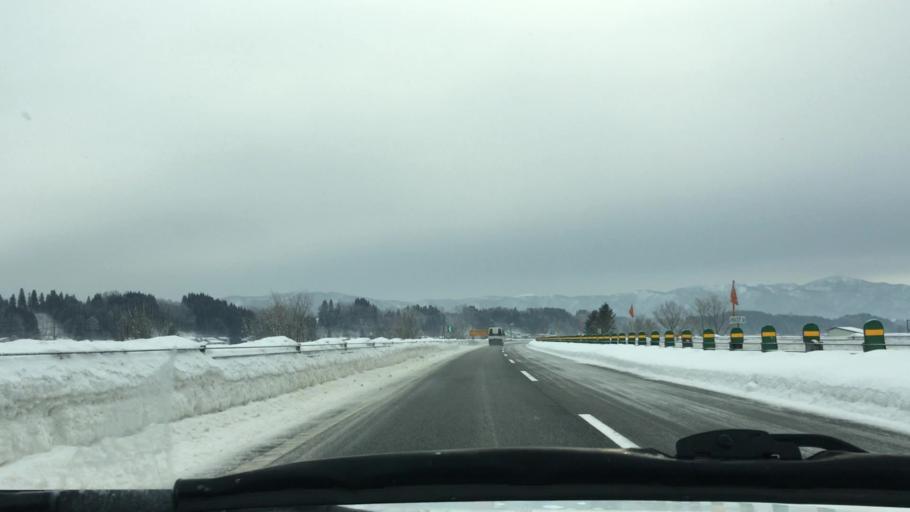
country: JP
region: Akita
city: Hanawa
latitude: 40.2992
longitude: 140.7492
